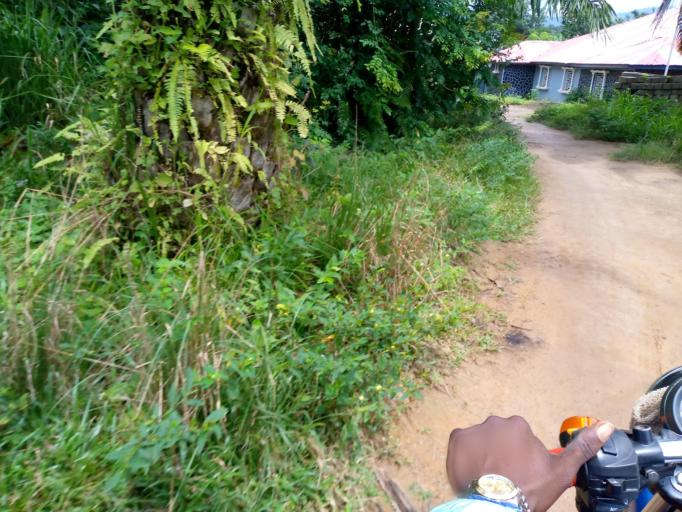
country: SL
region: Eastern Province
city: Kenema
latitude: 7.8786
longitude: -11.1691
